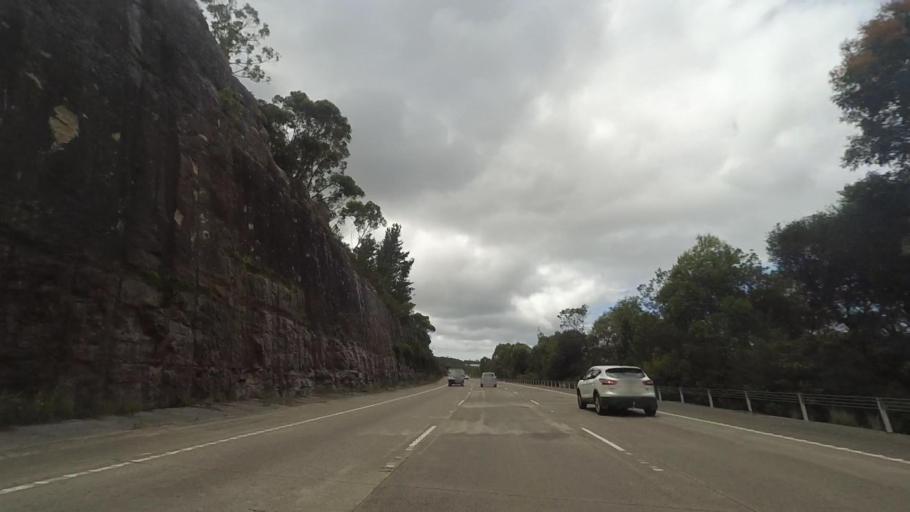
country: AU
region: New South Wales
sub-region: Gosford Shire
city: Point Clare
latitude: -33.4324
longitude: 151.2707
